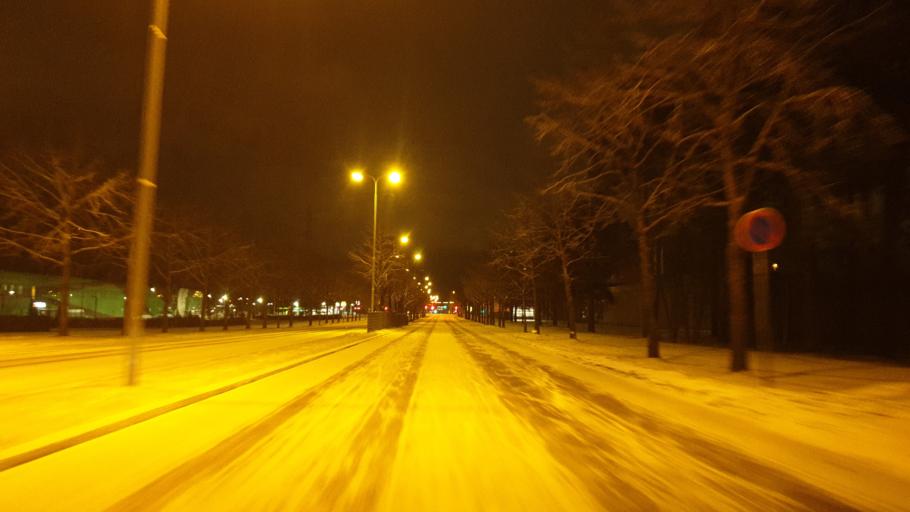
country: FI
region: Northern Ostrobothnia
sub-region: Oulu
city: Oulu
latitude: 64.9929
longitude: 25.4652
